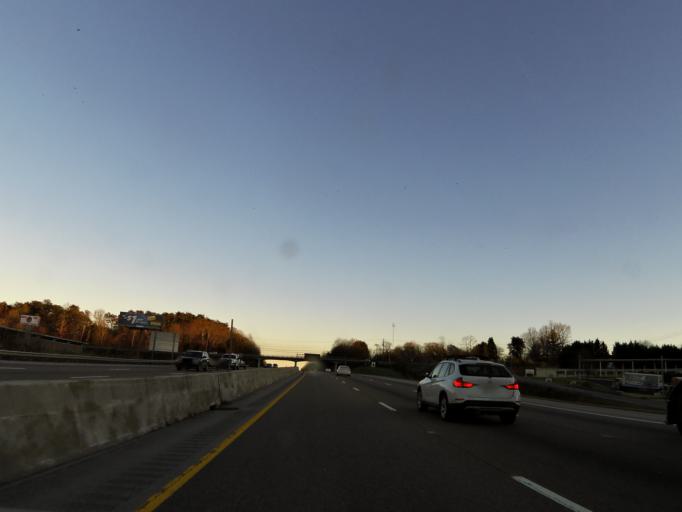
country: US
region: Tennessee
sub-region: Knox County
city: Knoxville
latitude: 36.0180
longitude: -83.9883
